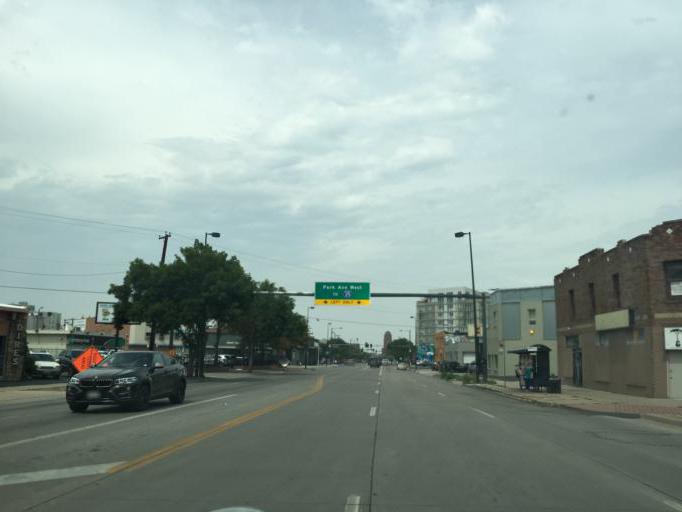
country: US
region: Colorado
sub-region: Denver County
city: Denver
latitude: 39.7530
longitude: -104.9874
